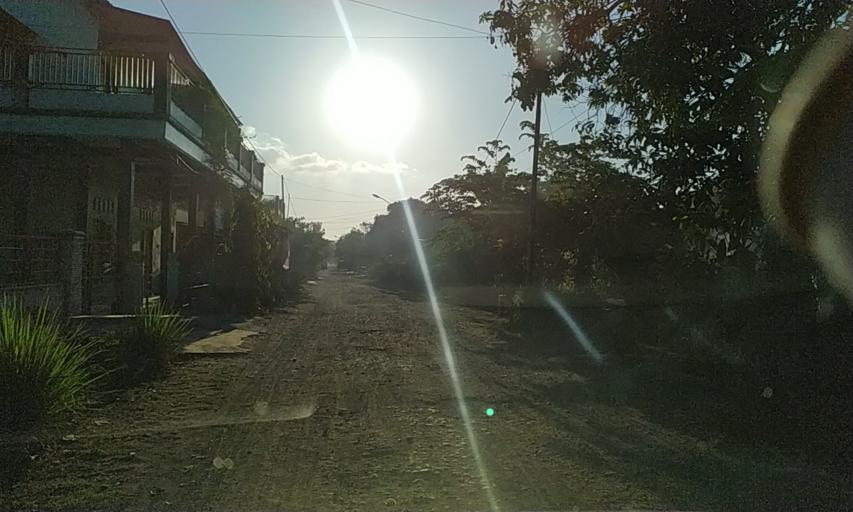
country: ID
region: Central Java
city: Cikalong
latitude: -7.4826
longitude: 108.7928
